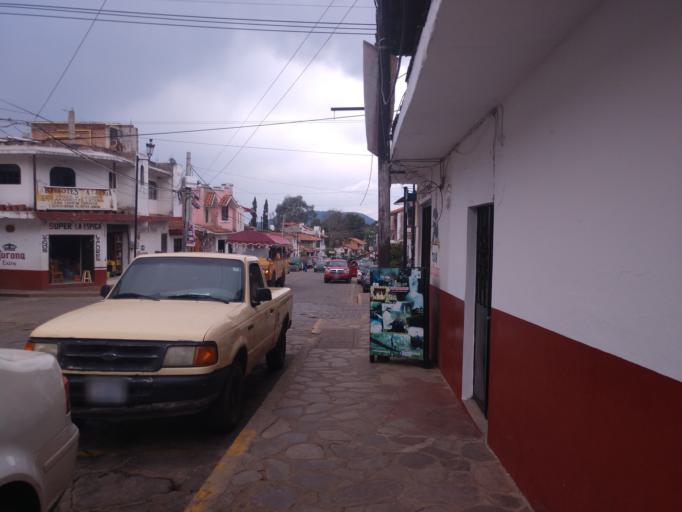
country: MX
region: Jalisco
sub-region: Mazamitla
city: Mazamitla
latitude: 19.9168
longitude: -103.0215
